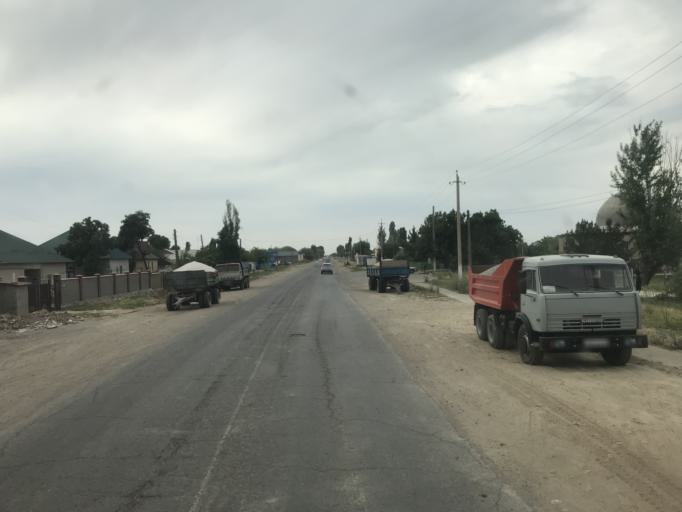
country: KZ
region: Ongtustik Qazaqstan
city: Asykata
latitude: 40.9015
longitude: 68.3583
